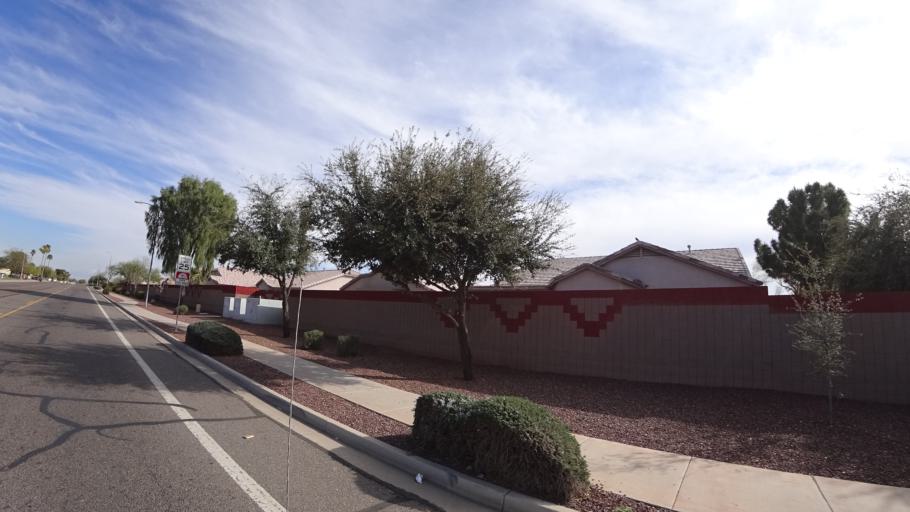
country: US
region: Arizona
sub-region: Maricopa County
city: Tolleson
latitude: 33.4281
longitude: -112.2974
